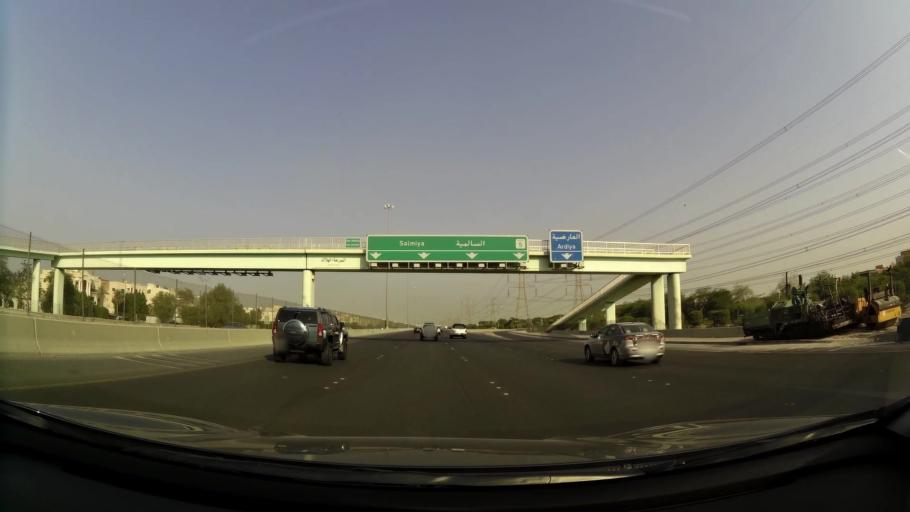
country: KW
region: Al Asimah
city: Ar Rabiyah
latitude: 29.2979
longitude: 47.8911
